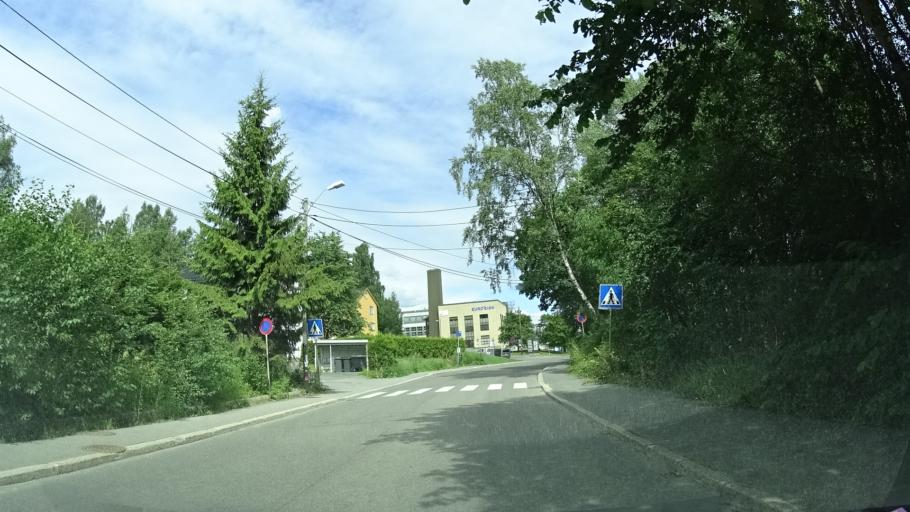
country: NO
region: Oslo
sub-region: Oslo
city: Oslo
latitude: 59.9627
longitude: 10.7693
